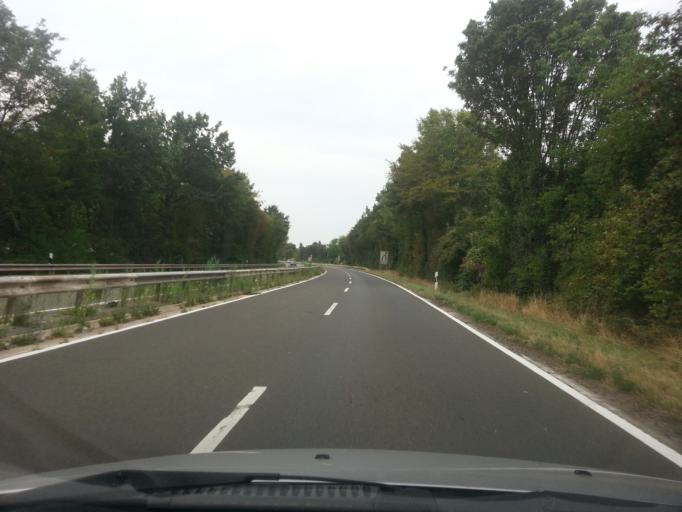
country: DE
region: Rheinland-Pfalz
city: Worms
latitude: 49.6183
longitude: 8.3607
